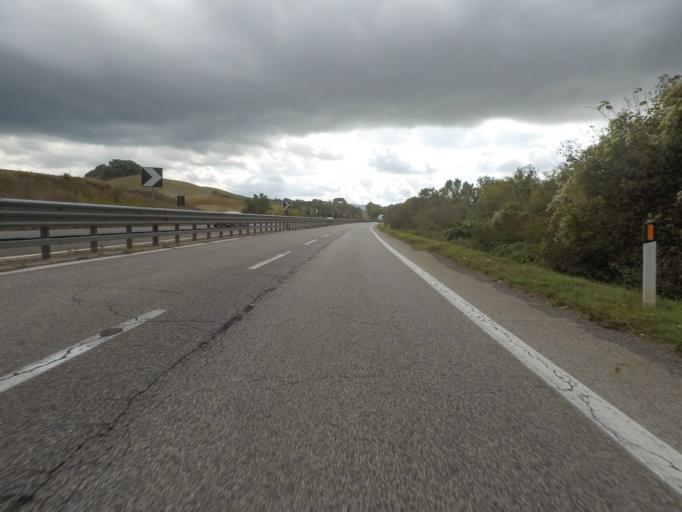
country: IT
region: Tuscany
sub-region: Provincia di Siena
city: Rapolano Terme
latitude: 43.3206
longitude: 11.5701
